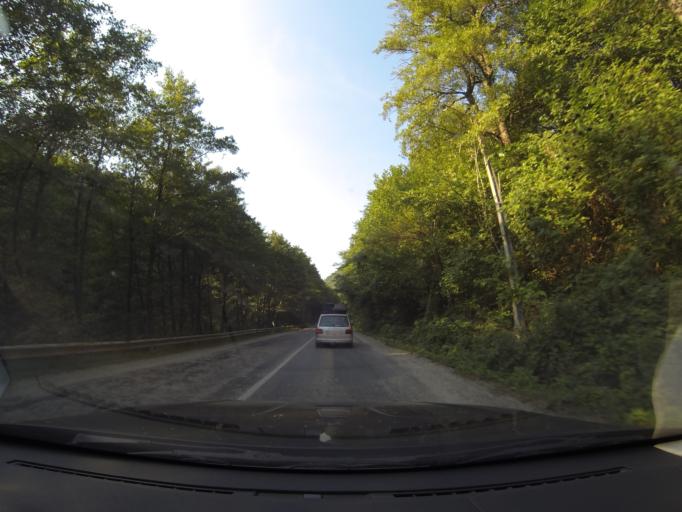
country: RO
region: Arges
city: Poenari
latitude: 45.3393
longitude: 24.6369
